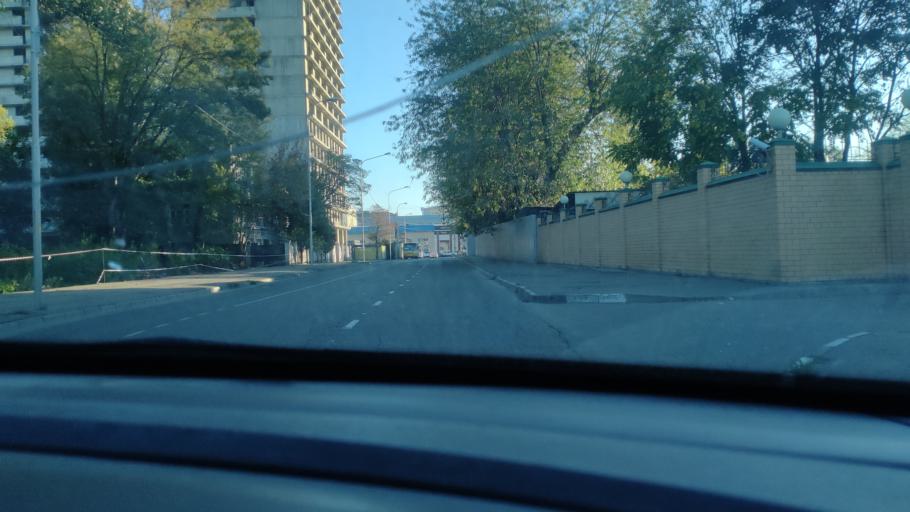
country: RU
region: Krasnodarskiy
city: Krasnodar
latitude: 45.0431
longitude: 38.9681
